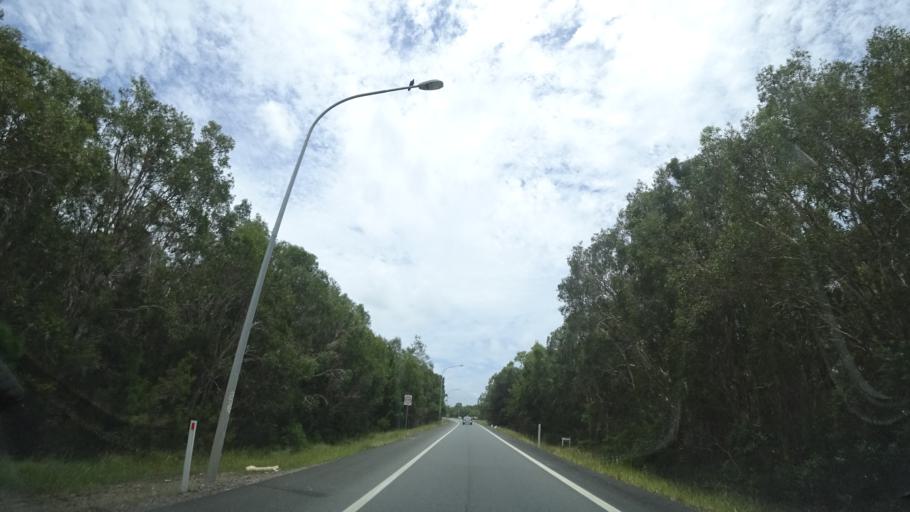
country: AU
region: Queensland
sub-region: Sunshine Coast
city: Mooloolaba
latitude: -26.6911
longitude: 153.1084
